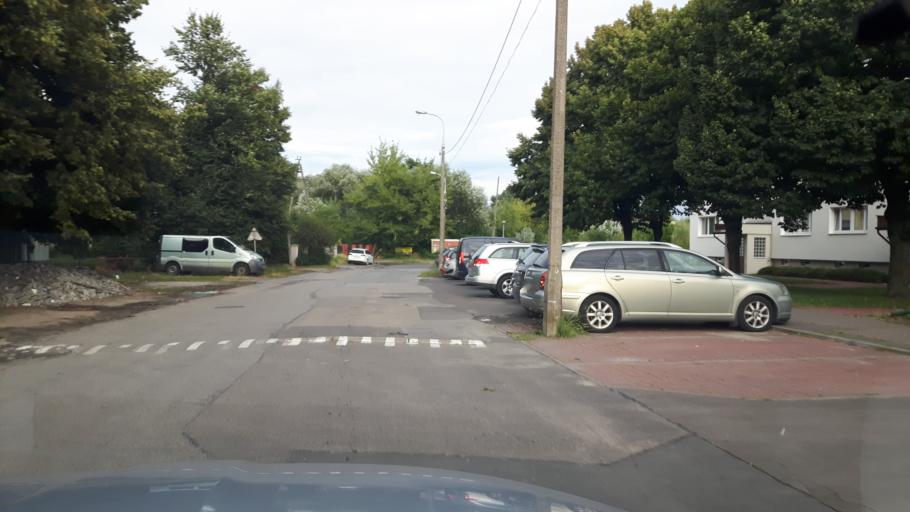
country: PL
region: Masovian Voivodeship
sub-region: Powiat wolominski
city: Marki
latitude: 52.3293
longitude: 21.1034
